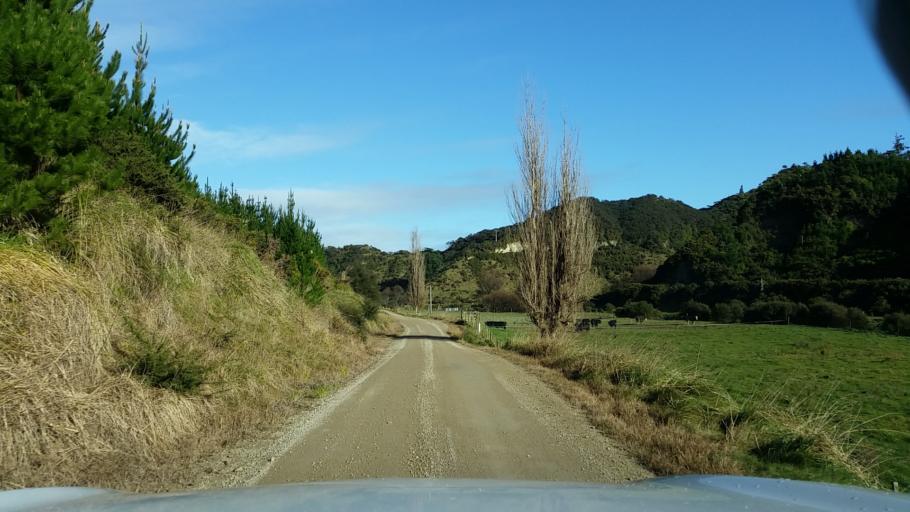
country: NZ
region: Taranaki
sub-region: South Taranaki District
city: Patea
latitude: -39.6960
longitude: 174.7435
